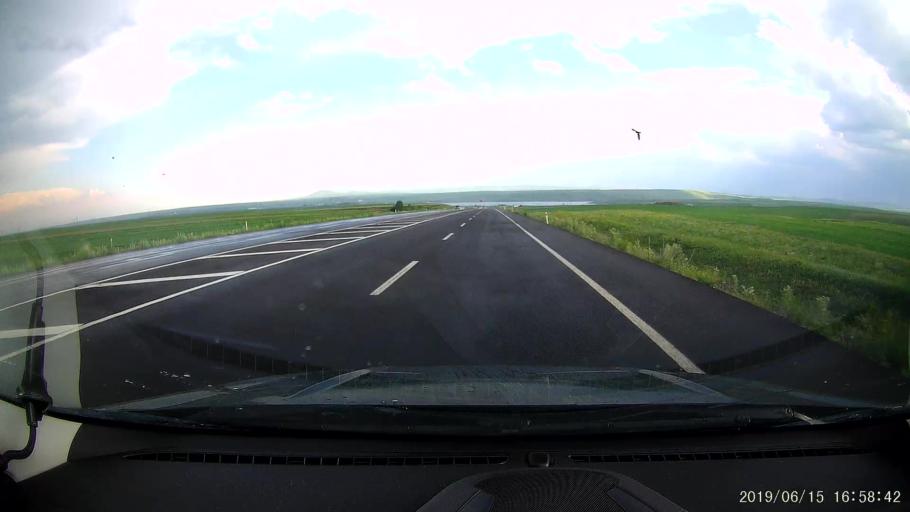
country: TR
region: Kars
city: Susuz
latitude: 40.7614
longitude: 43.1456
